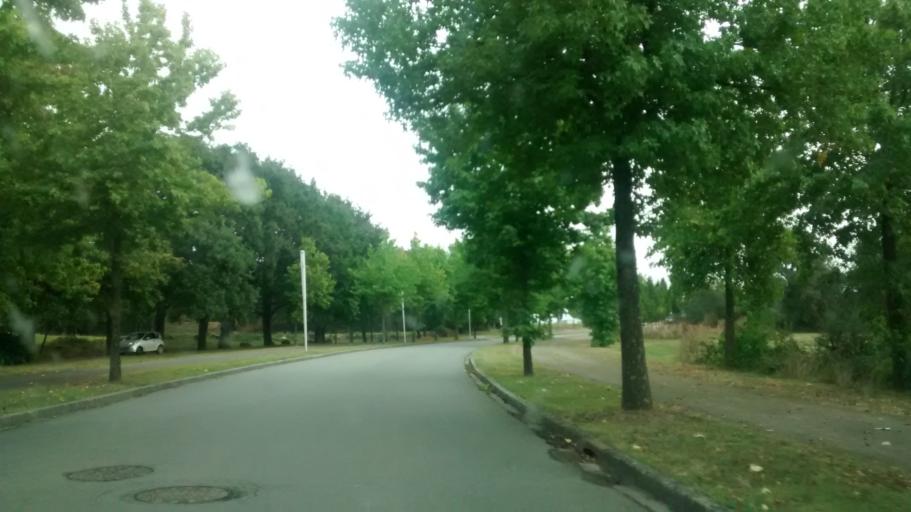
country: FR
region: Brittany
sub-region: Departement d'Ille-et-Vilaine
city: Saint-Jacques-de-la-Lande
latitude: 48.0519
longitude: -1.7397
